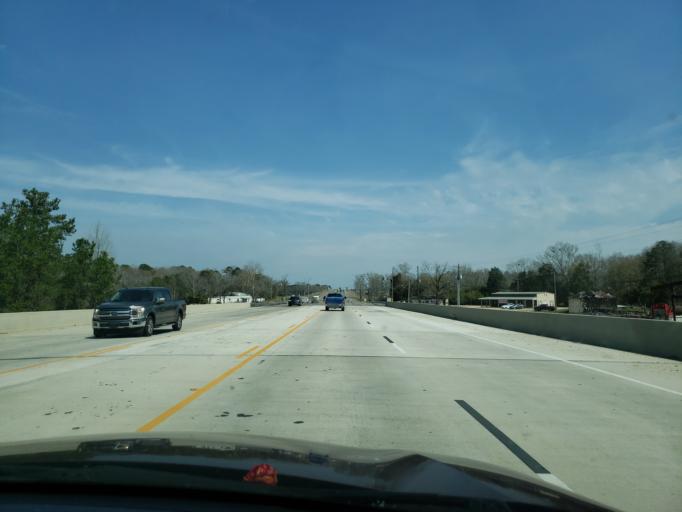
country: US
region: Alabama
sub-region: Elmore County
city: Elmore
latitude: 32.5344
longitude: -86.3212
